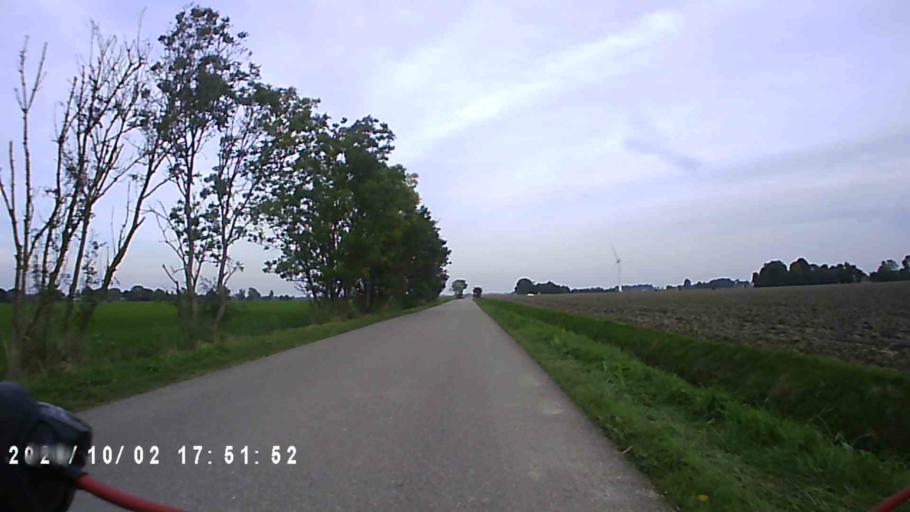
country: NL
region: Groningen
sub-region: Gemeente Zuidhorn
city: Oldehove
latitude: 53.3359
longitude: 6.4186
